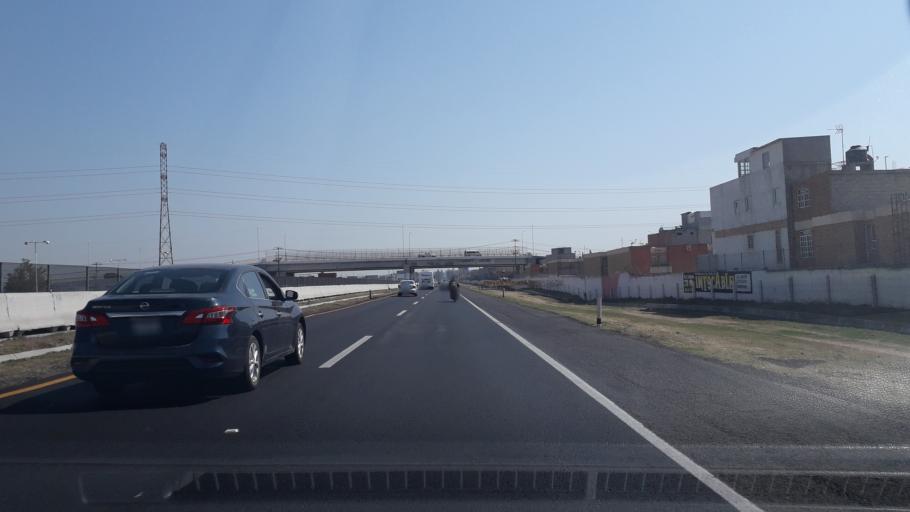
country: MX
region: Mexico
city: Santo Tomas Chiconautla
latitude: 19.6304
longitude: -99.0233
